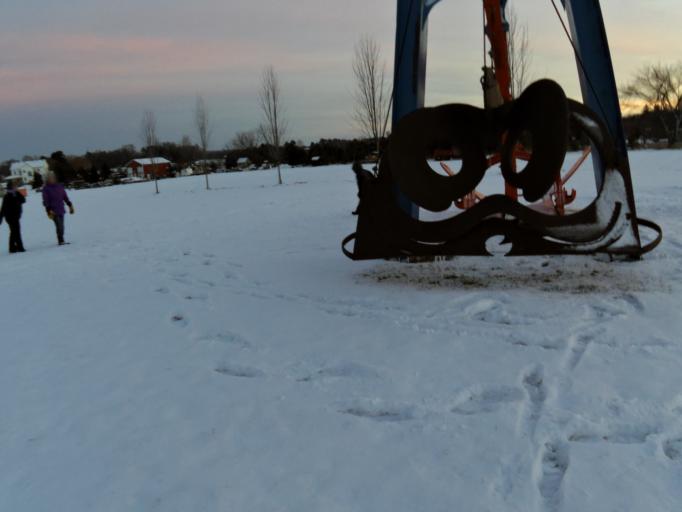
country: US
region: Minnesota
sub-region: Chisago County
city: Shafer
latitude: 45.3807
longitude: -92.7080
